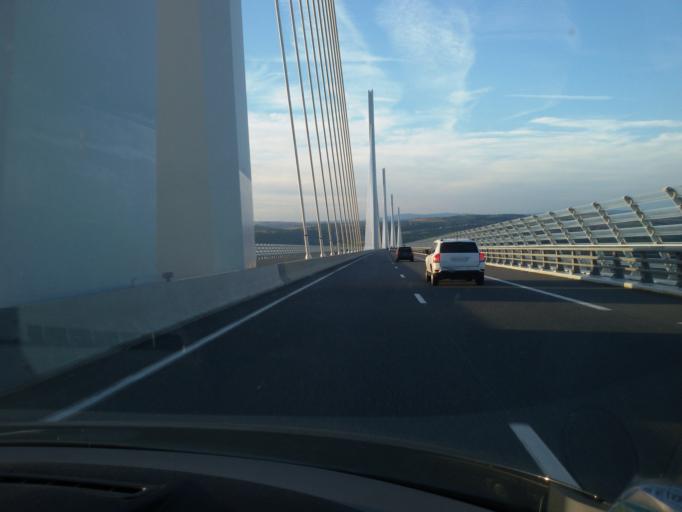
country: FR
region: Midi-Pyrenees
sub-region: Departement de l'Aveyron
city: Creissels
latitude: 44.0769
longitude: 3.0230
